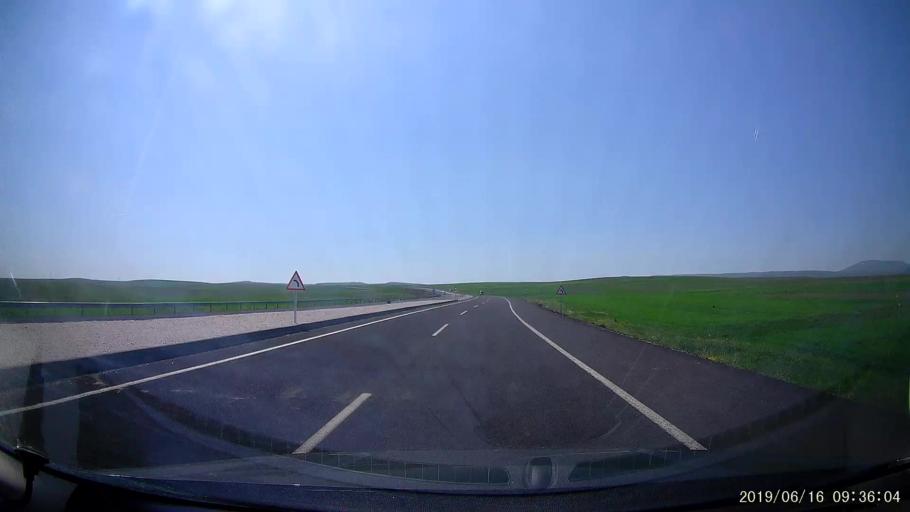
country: TR
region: Kars
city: Kars
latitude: 40.5622
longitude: 43.1661
